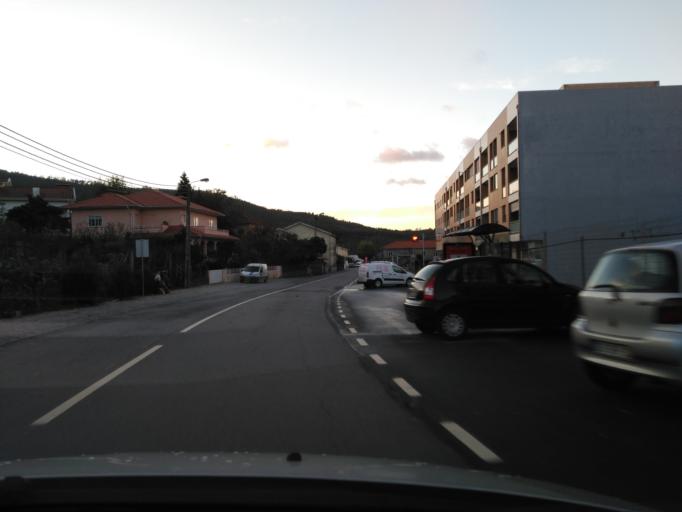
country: PT
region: Braga
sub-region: Braga
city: Braga
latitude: 41.5311
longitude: -8.4100
